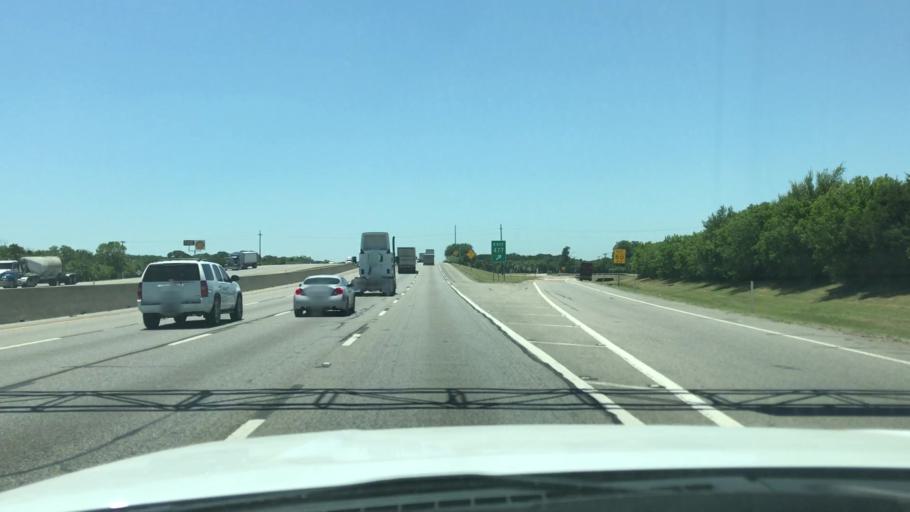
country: US
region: Texas
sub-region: Dallas County
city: Balch Springs
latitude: 32.6839
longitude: -96.6538
